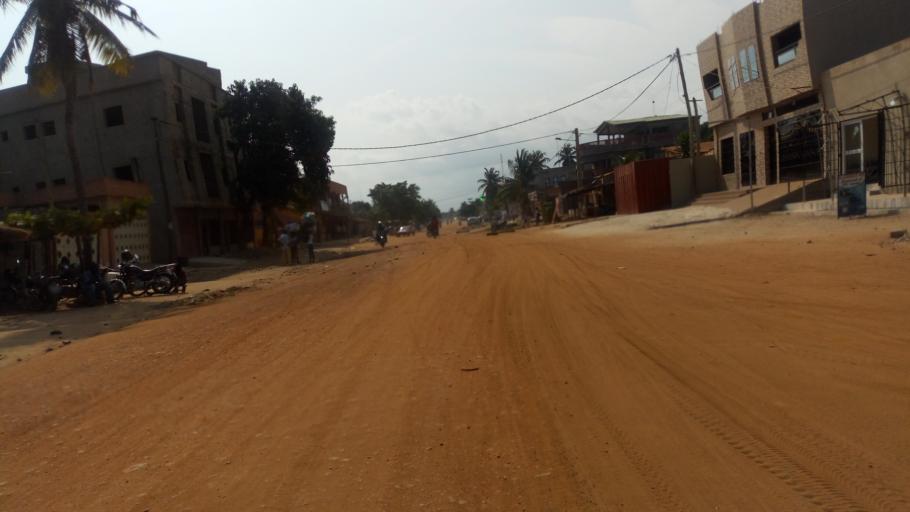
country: TG
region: Maritime
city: Lome
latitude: 6.1916
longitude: 1.1822
